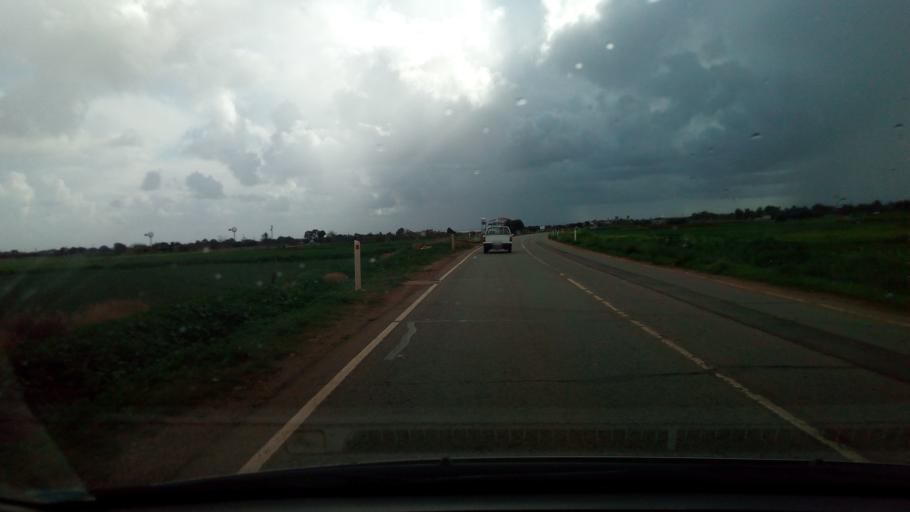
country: CY
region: Ammochostos
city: Liopetri
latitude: 34.9856
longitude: 33.8944
